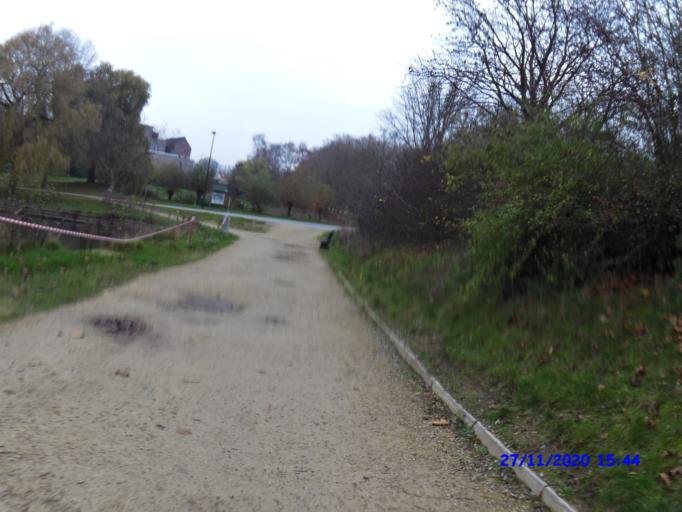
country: BE
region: Flanders
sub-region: Provincie Vlaams-Brabant
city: Dilbeek
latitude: 50.8248
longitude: 4.2781
